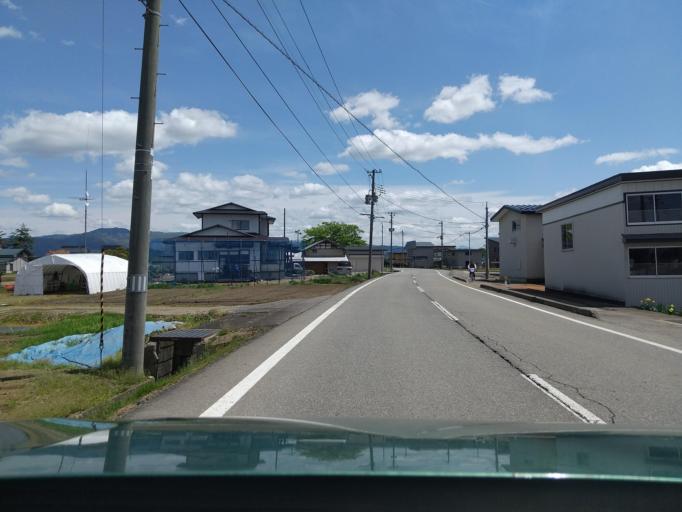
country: JP
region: Akita
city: Omagari
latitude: 39.3843
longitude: 140.5162
